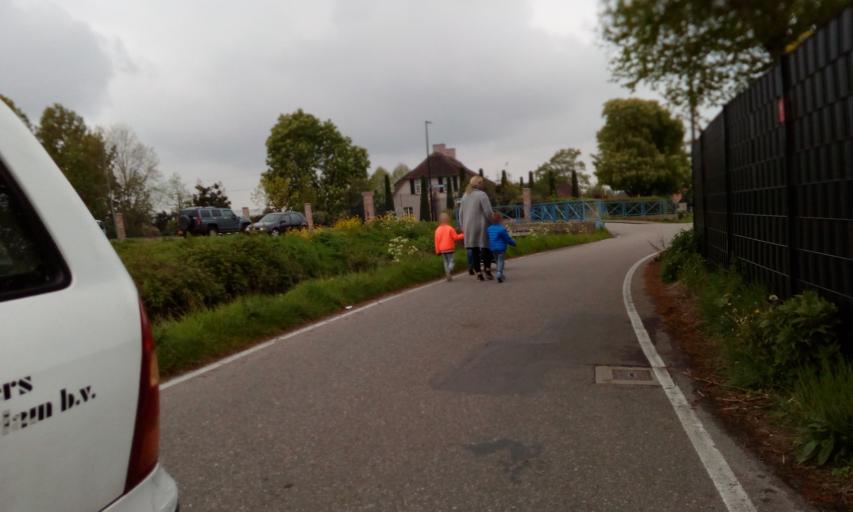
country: NL
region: South Holland
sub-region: Gemeente Schiedam
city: Schiedam
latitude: 51.9384
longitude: 4.3987
